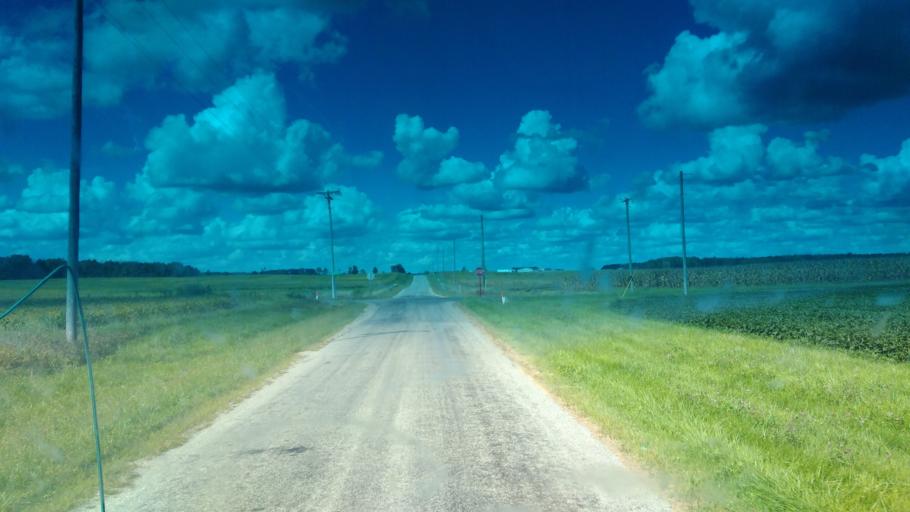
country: US
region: Ohio
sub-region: Union County
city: Richwood
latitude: 40.4596
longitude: -83.4950
